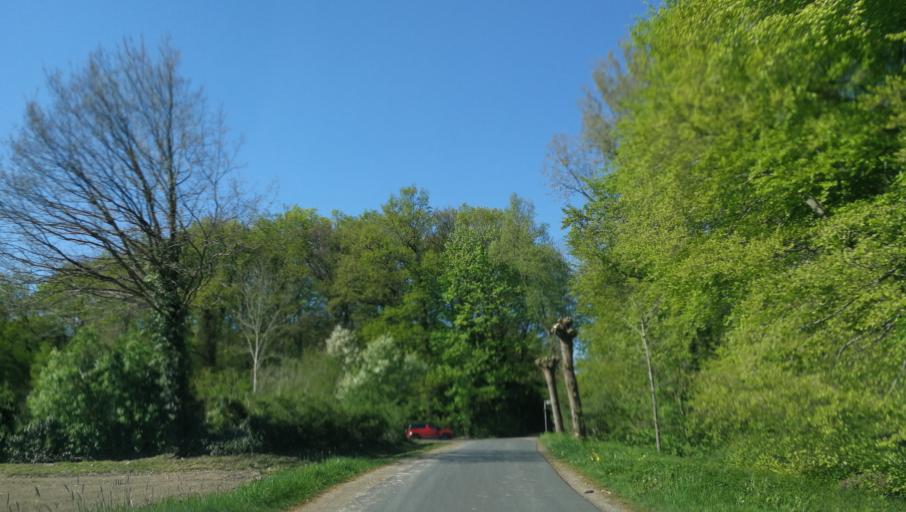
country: DE
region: North Rhine-Westphalia
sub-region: Regierungsbezirk Munster
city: Muenster
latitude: 51.9408
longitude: 7.5451
